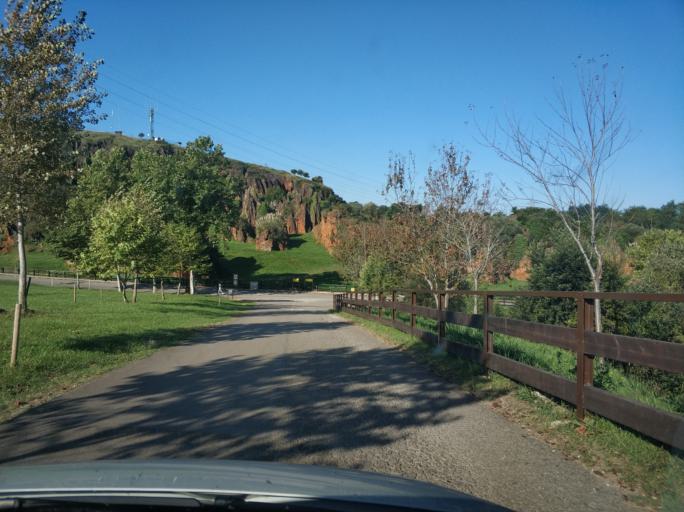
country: ES
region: Cantabria
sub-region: Provincia de Cantabria
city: Penagos
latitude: 43.3511
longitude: -3.8422
